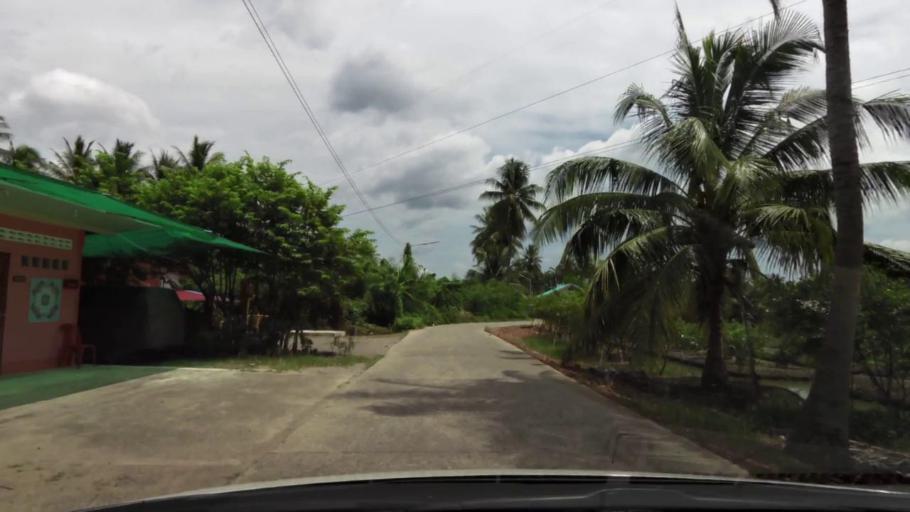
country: TH
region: Ratchaburi
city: Damnoen Saduak
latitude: 13.5185
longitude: 100.0061
